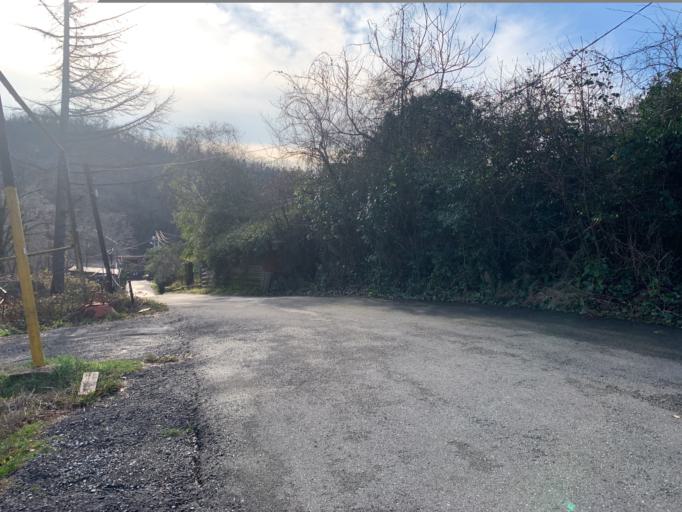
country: RU
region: Krasnodarskiy
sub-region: Sochi City
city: Lazarevskoye
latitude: 43.9240
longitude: 39.3231
